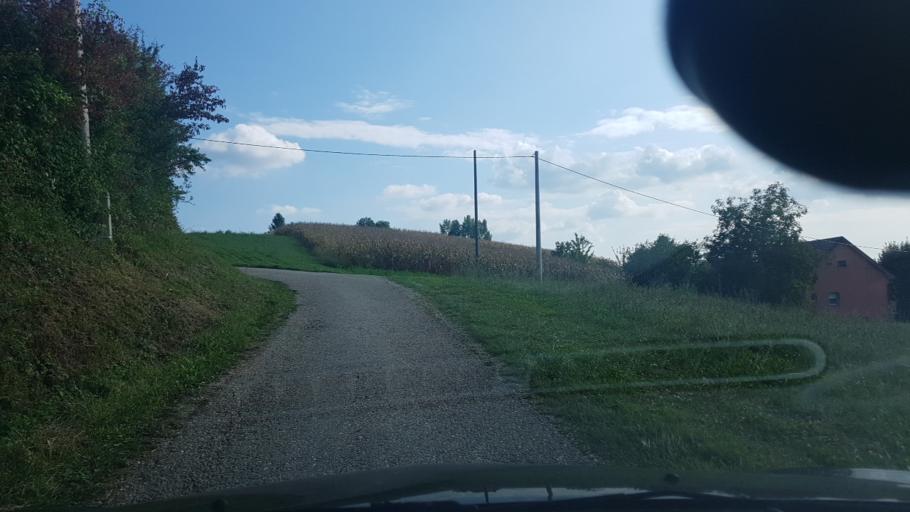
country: HR
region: Krapinsko-Zagorska
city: Radoboj
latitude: 46.1577
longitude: 15.9346
